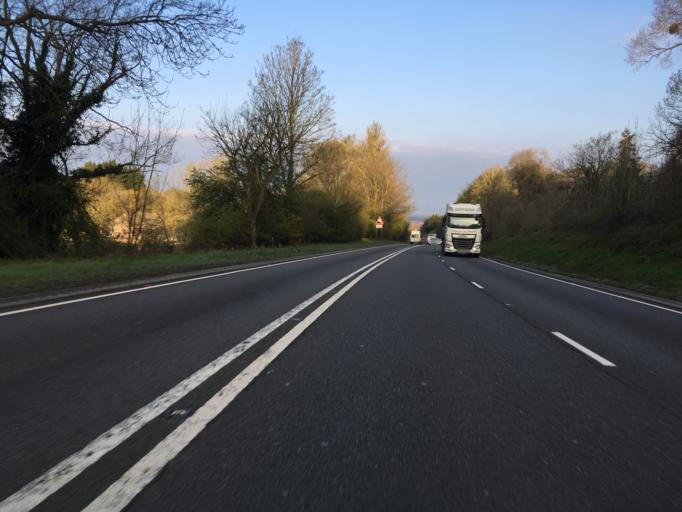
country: GB
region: England
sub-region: Gloucestershire
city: Shurdington
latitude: 51.8403
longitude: -2.1115
